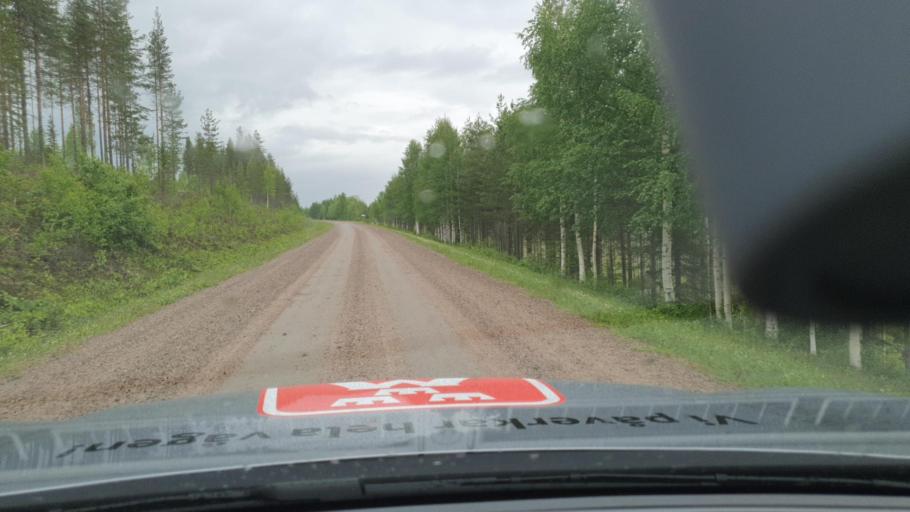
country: SE
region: Norrbotten
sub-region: Overkalix Kommun
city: OEverkalix
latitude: 66.5949
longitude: 22.7484
